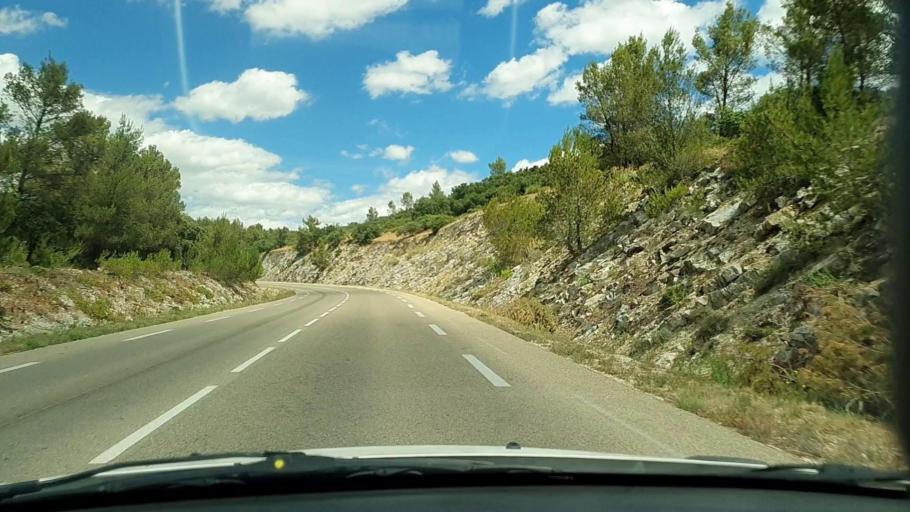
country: FR
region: Languedoc-Roussillon
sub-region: Departement du Gard
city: Poulx
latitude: 43.8855
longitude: 4.4172
